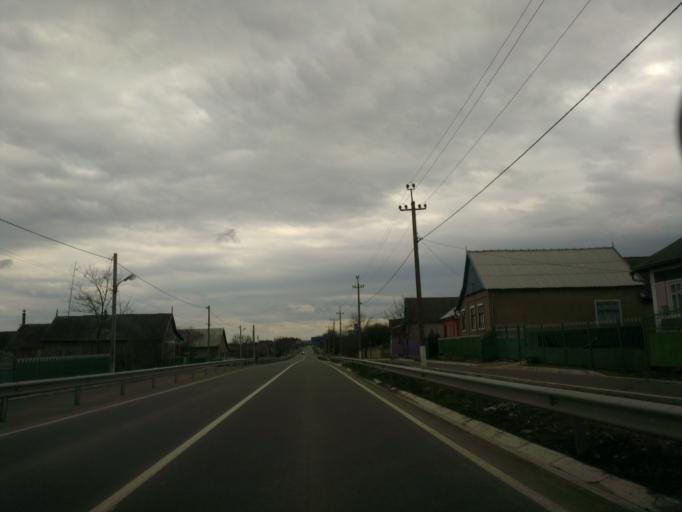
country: MD
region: Cimislia
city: Cimislia
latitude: 46.6254
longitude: 28.7227
